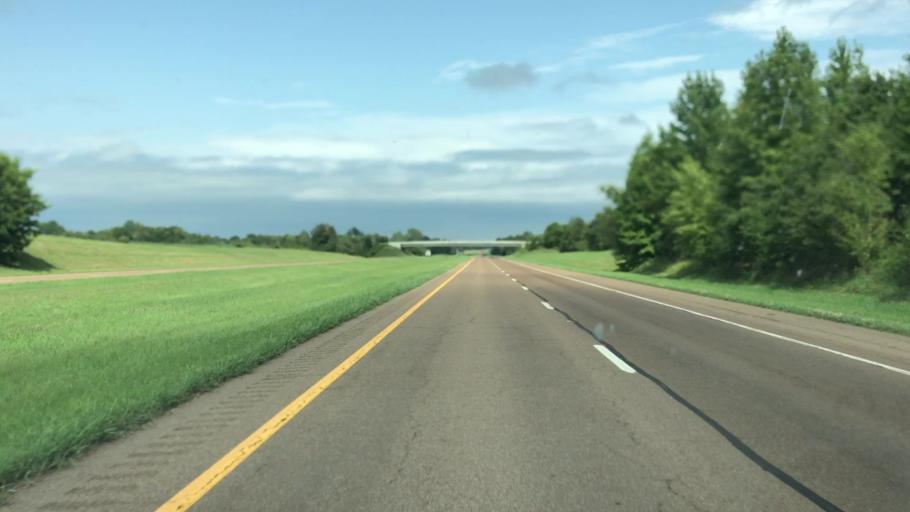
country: US
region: Tennessee
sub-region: Obion County
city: Union City
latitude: 36.4638
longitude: -88.9789
